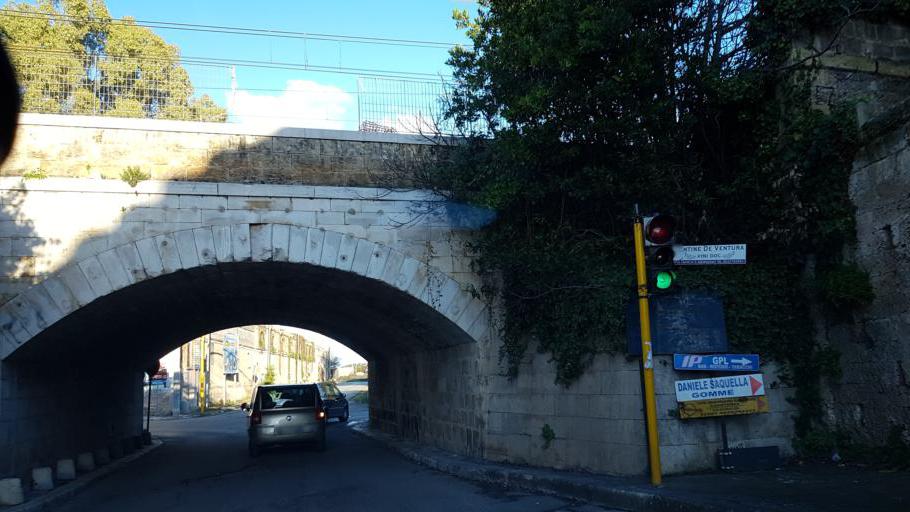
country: IT
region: Apulia
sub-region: Provincia di Lecce
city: Squinzano
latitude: 40.4378
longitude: 18.0473
